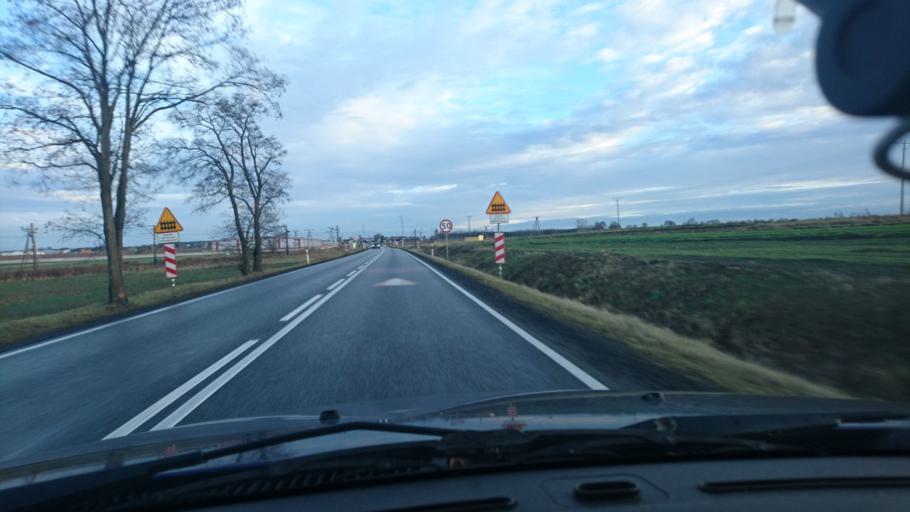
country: PL
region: Greater Poland Voivodeship
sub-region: Powiat kepinski
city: Slupia pod Kepnem
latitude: 51.2334
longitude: 18.0620
